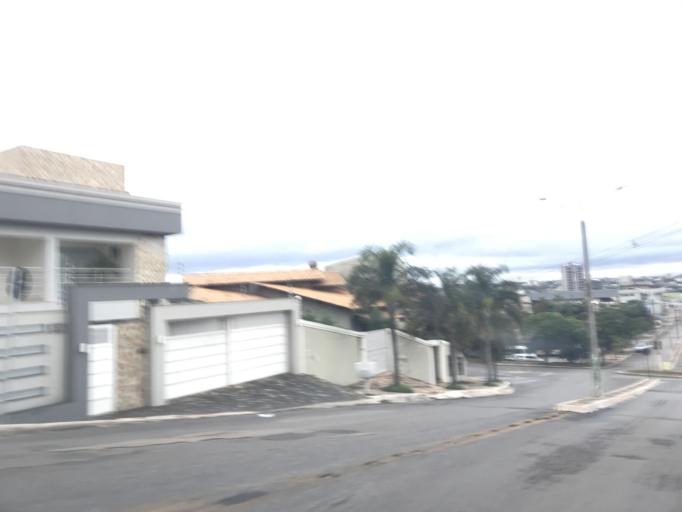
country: BR
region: Goias
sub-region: Luziania
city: Luziania
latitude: -16.2561
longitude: -47.9604
